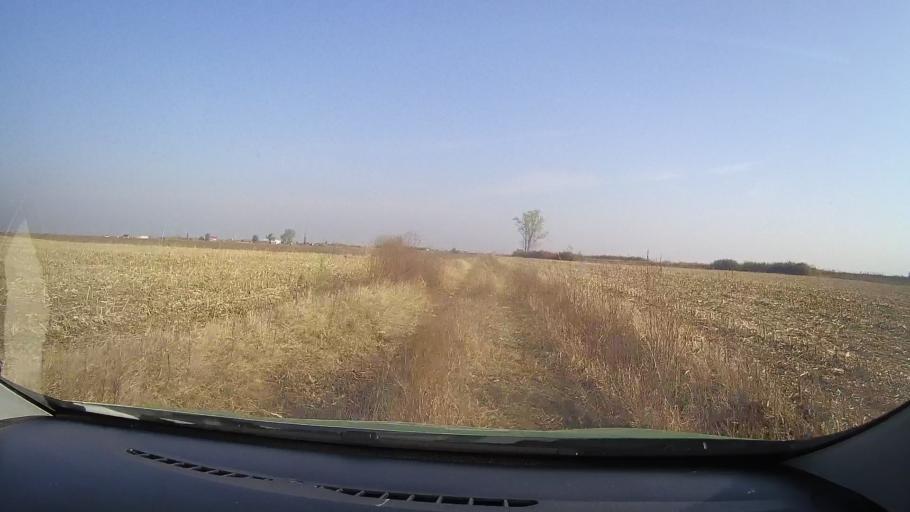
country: RO
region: Arad
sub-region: Comuna Pilu
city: Pilu
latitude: 46.5598
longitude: 21.3455
